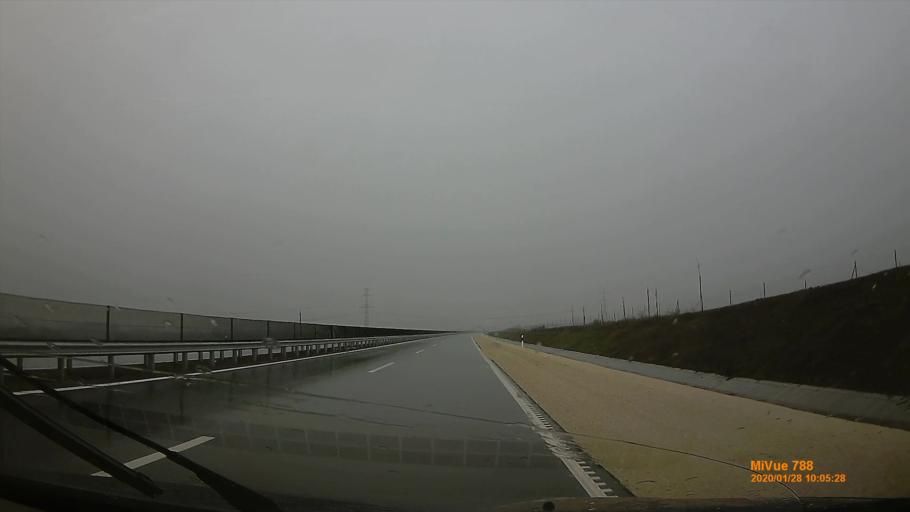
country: HU
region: Pest
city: Albertirsa
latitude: 47.2782
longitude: 19.5942
